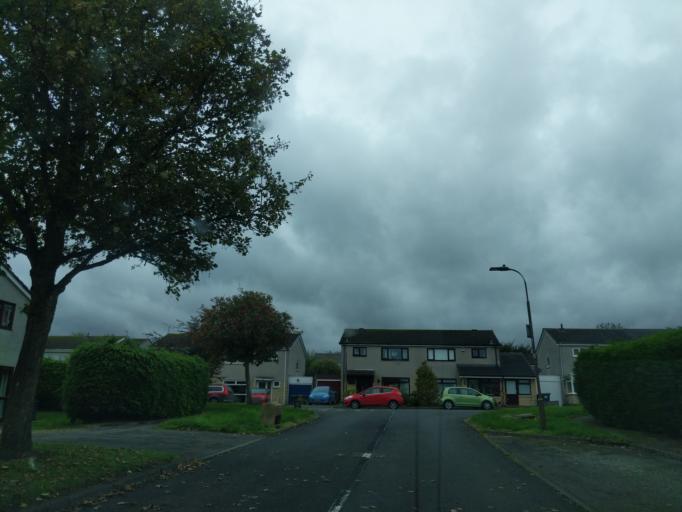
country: GB
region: Scotland
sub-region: Edinburgh
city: Balerno
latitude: 55.8784
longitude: -3.3464
